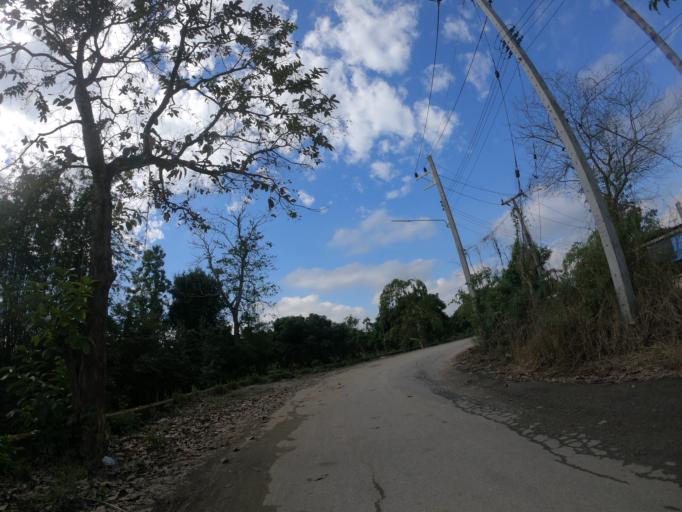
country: TH
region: Chiang Mai
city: Saraphi
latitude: 18.7033
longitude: 98.9769
